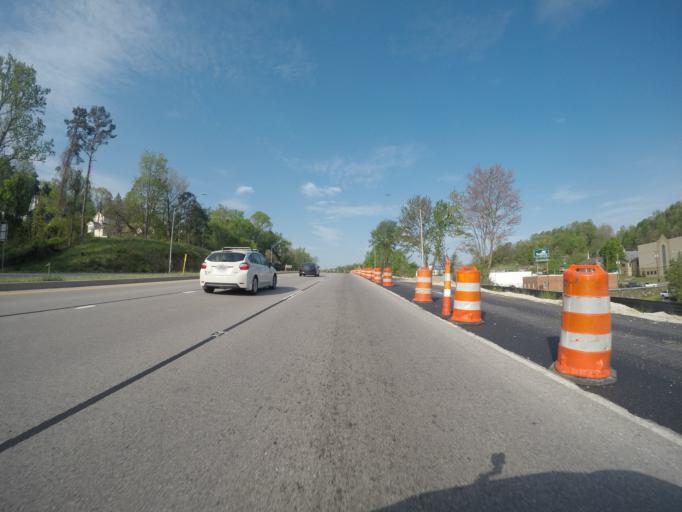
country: US
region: West Virginia
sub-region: Kanawha County
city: Charleston
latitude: 38.3426
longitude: -81.6605
